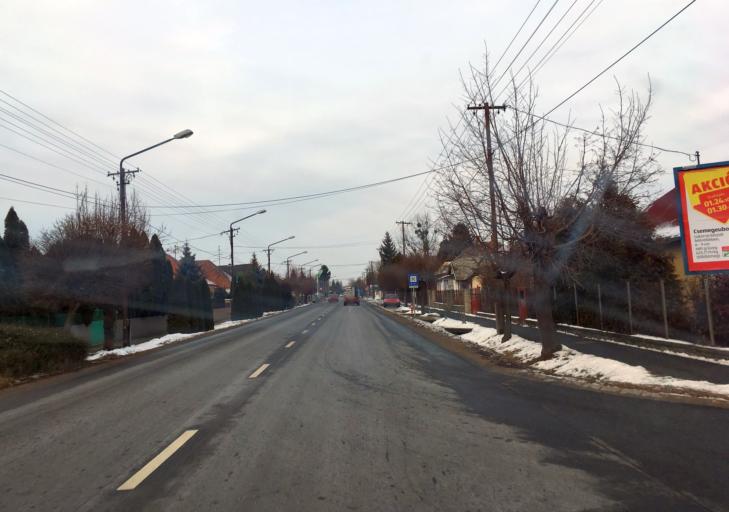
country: HU
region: Gyor-Moson-Sopron
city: Mosonmagyarovar
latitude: 47.8638
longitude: 17.2674
